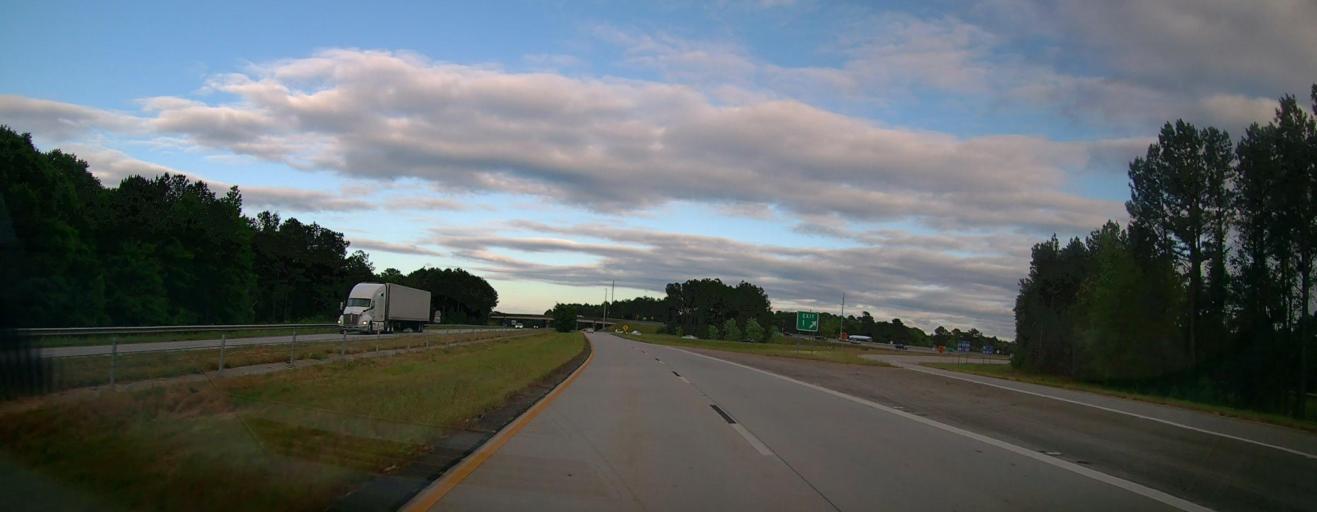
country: US
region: Georgia
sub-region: Oconee County
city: Watkinsville
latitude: 33.9141
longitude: -83.4562
